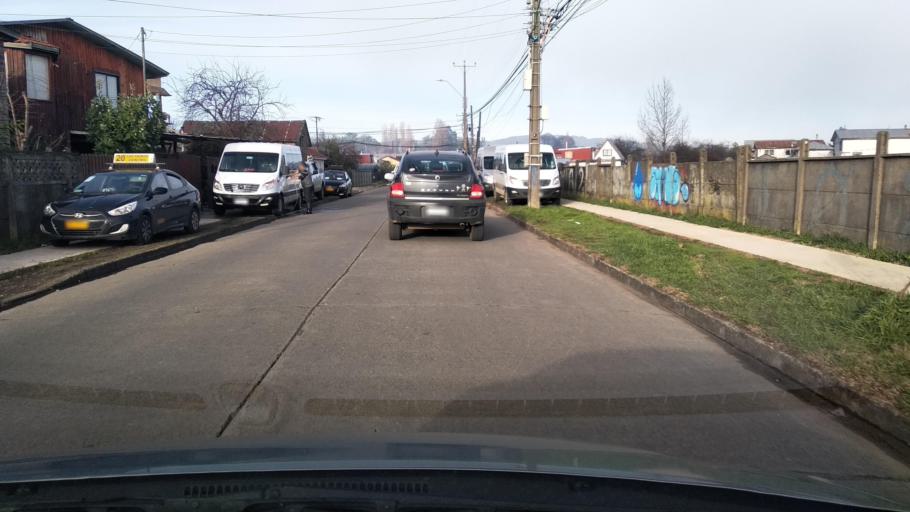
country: CL
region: Los Lagos
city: Las Animas
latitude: -39.8093
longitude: -73.2243
